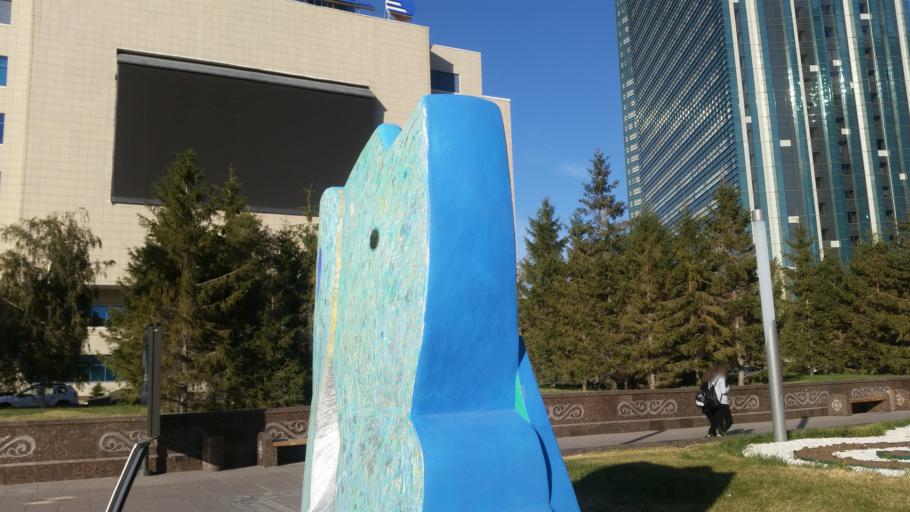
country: KZ
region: Astana Qalasy
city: Astana
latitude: 51.1298
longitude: 71.4210
